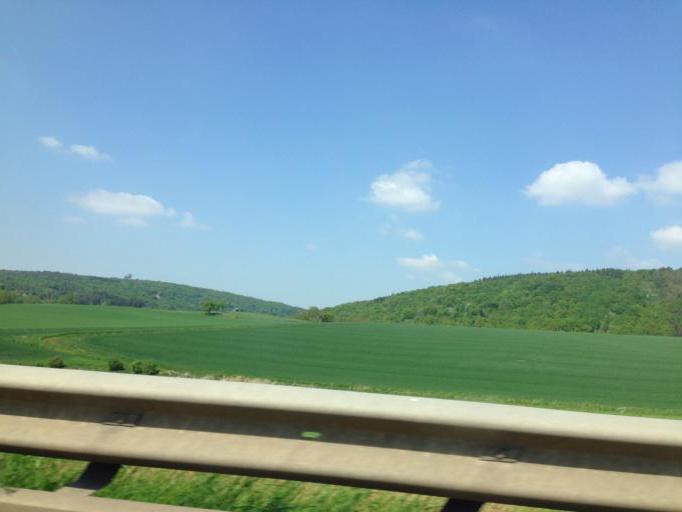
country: DE
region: North Rhine-Westphalia
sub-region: Regierungsbezirk Koln
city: Bad Munstereifel
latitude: 50.5508
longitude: 6.7246
